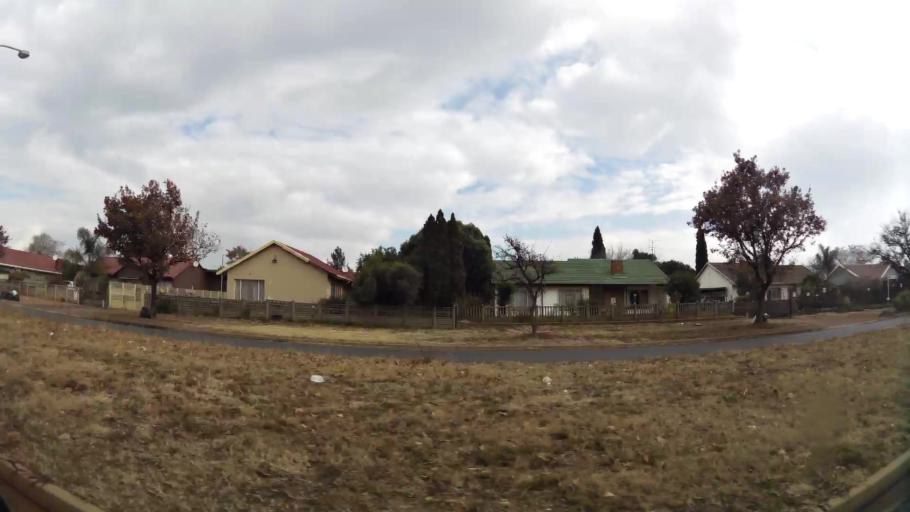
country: ZA
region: Gauteng
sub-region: Sedibeng District Municipality
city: Vanderbijlpark
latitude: -26.7217
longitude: 27.8630
